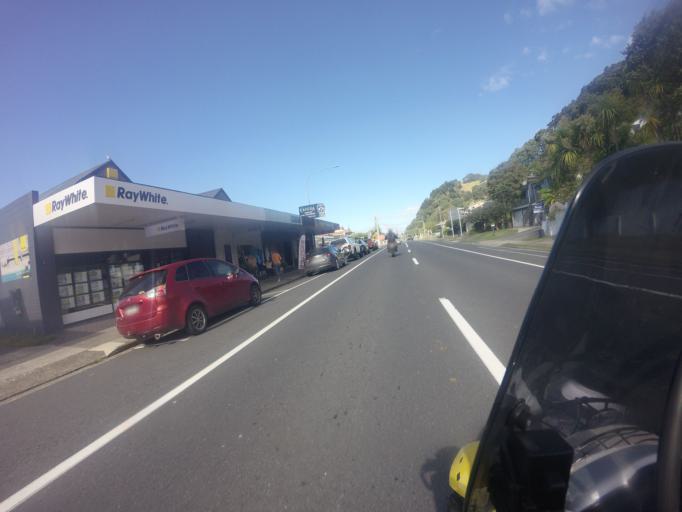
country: NZ
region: Bay of Plenty
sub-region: Whakatane District
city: Whakatane
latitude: -37.9643
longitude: 177.0358
